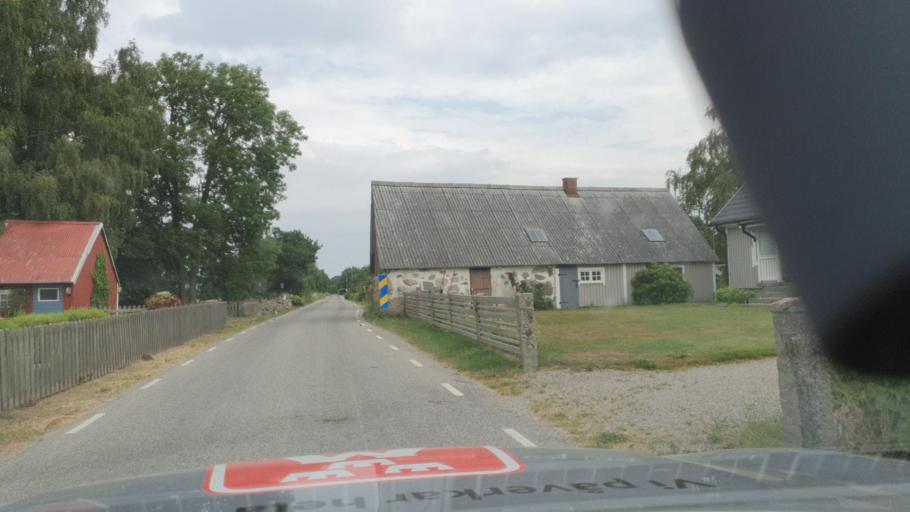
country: SE
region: Blekinge
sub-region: Solvesborgs Kommun
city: Soelvesborg
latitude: 56.0592
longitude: 14.6550
